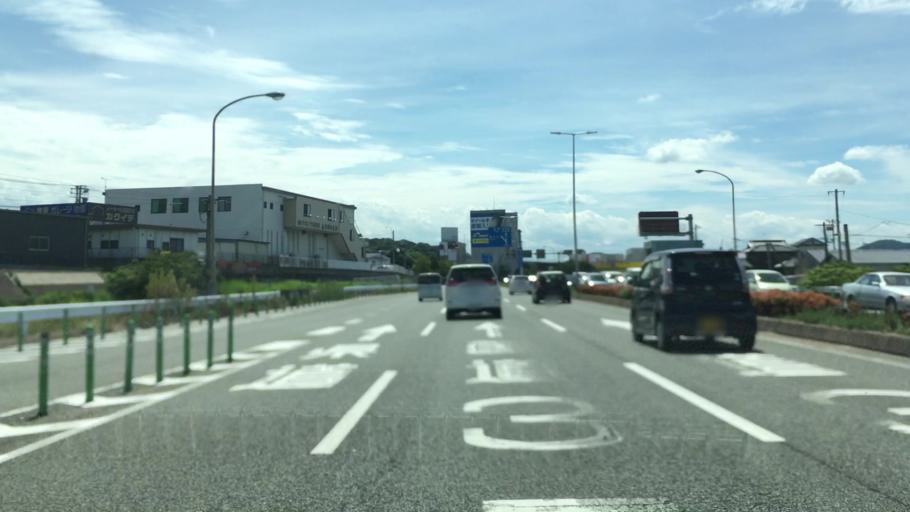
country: JP
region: Fukuoka
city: Onojo
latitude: 33.5295
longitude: 130.4932
